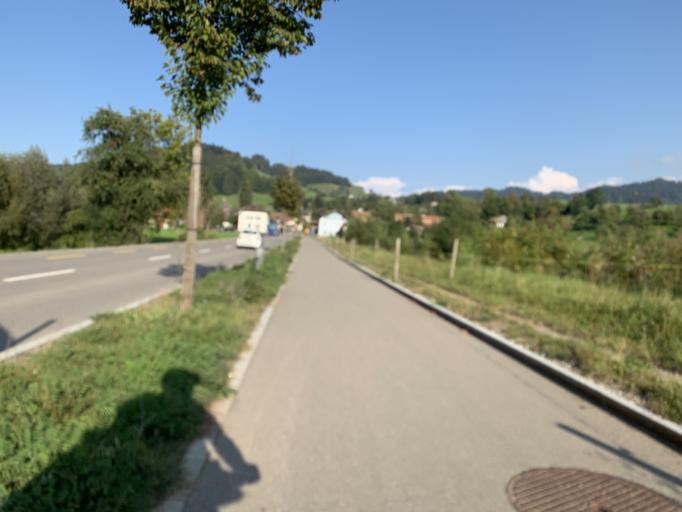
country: CH
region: Zurich
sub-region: Bezirk Hinwil
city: Baretswil
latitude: 47.3317
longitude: 8.8525
